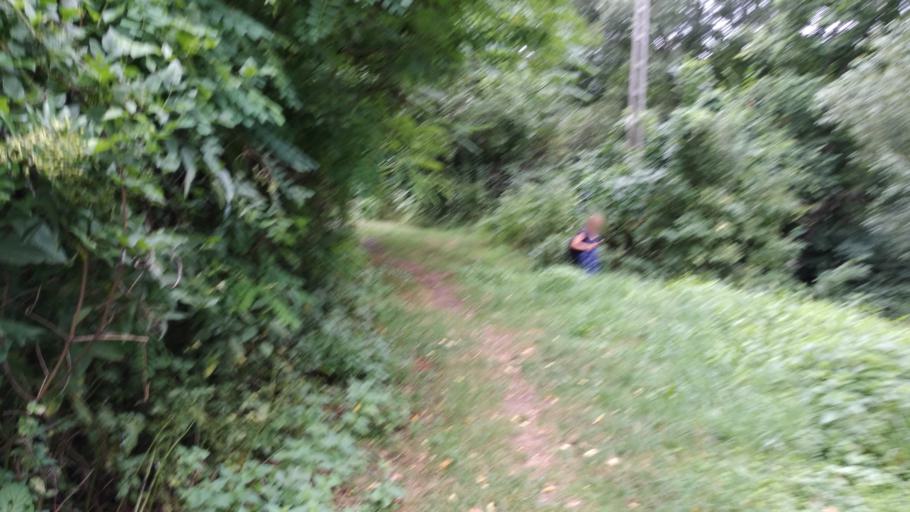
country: HU
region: Pest
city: Szob
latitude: 47.9350
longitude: 18.8335
